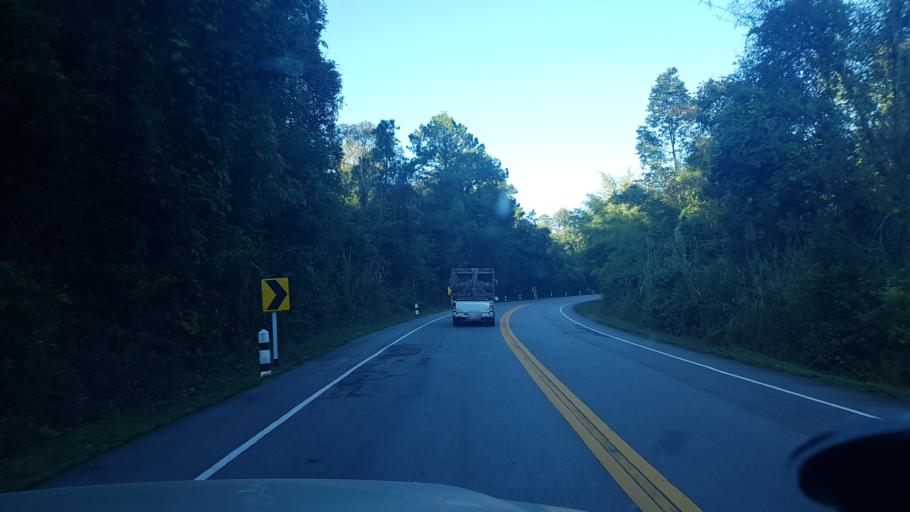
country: TH
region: Phetchabun
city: Nam Nao
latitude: 16.7002
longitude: 101.6208
